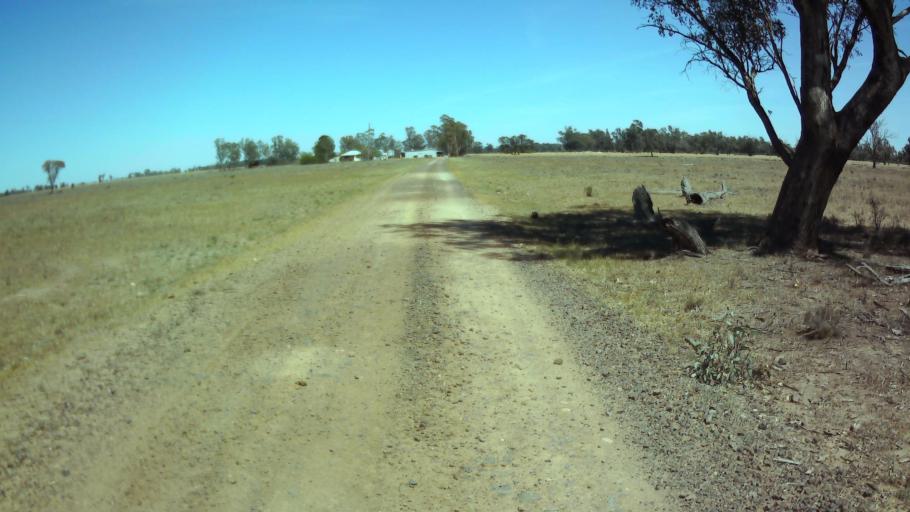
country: AU
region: New South Wales
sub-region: Weddin
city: Grenfell
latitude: -34.0482
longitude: 147.9210
